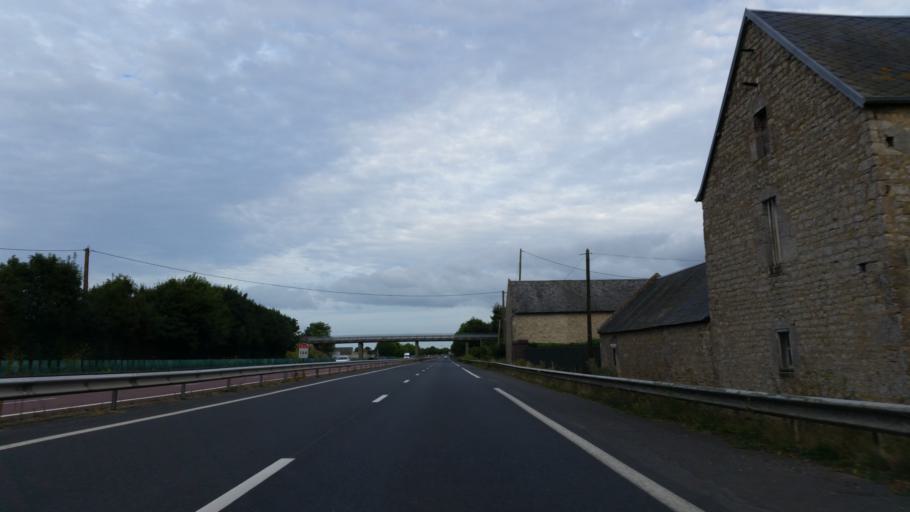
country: FR
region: Lower Normandy
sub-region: Departement du Calvados
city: Grandcamp-Maisy
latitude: 49.3425
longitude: -1.0428
